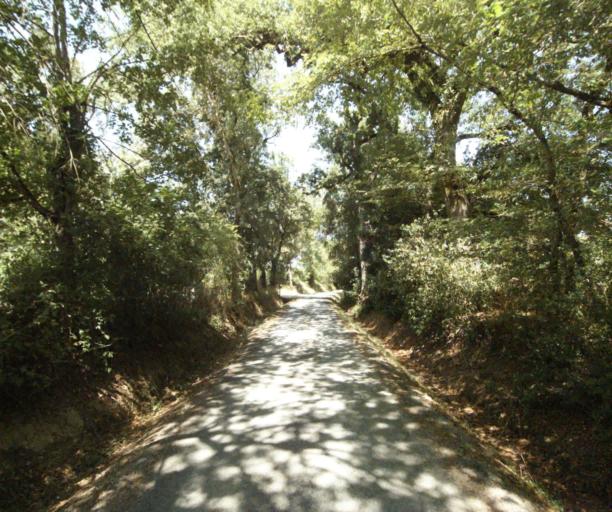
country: FR
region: Midi-Pyrenees
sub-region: Departement de la Haute-Garonne
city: Revel
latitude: 43.5030
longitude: 2.0003
